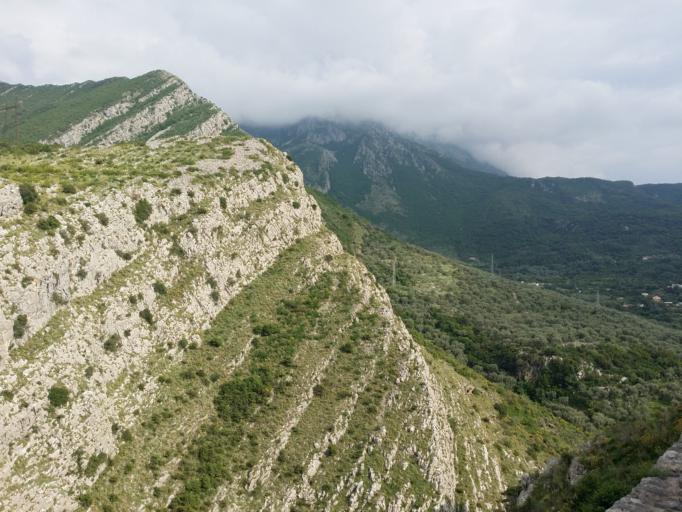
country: ME
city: Stari Bar
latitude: 42.0938
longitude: 19.1363
